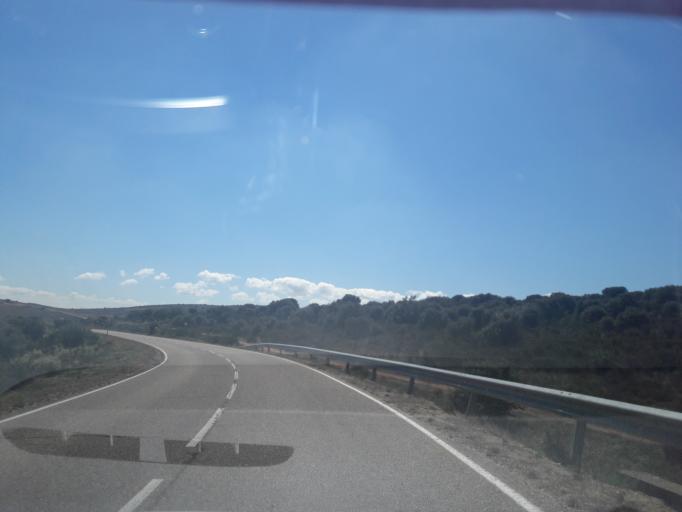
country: ES
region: Castille and Leon
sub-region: Provincia de Salamanca
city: Doninos de Salamanca
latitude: 40.9406
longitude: -5.7257
